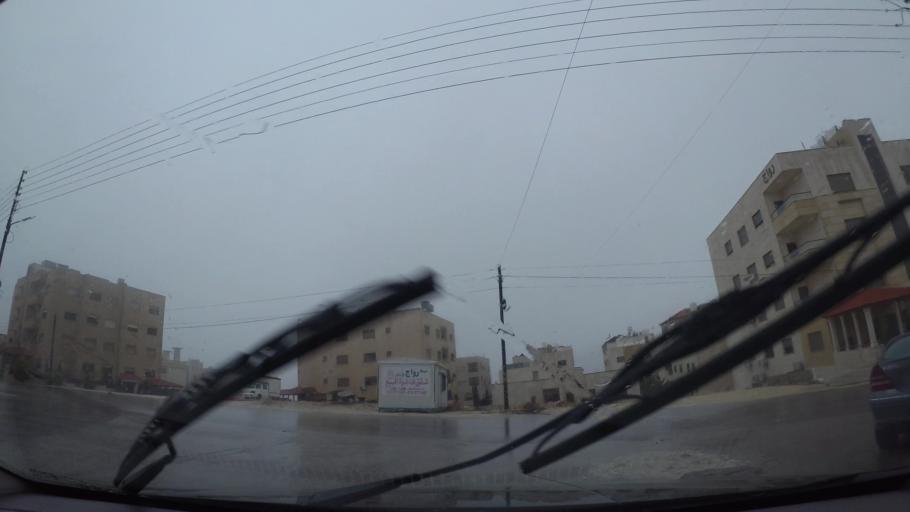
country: JO
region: Amman
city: Al Jubayhah
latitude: 32.0170
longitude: 35.8862
